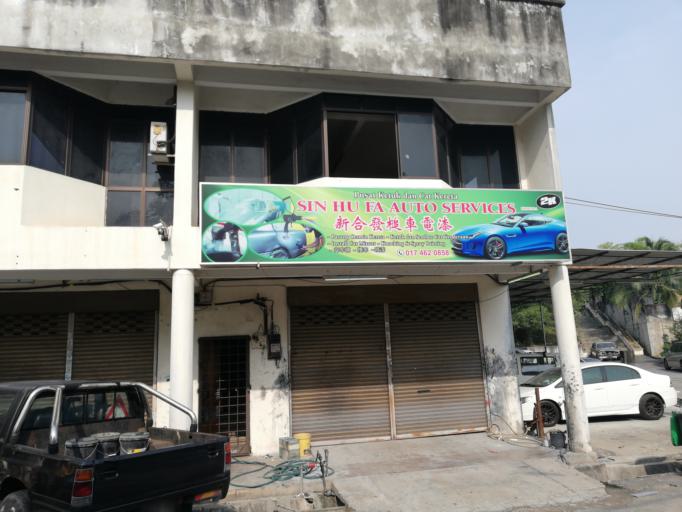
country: MY
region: Kedah
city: Kulim
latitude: 5.3731
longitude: 100.5405
